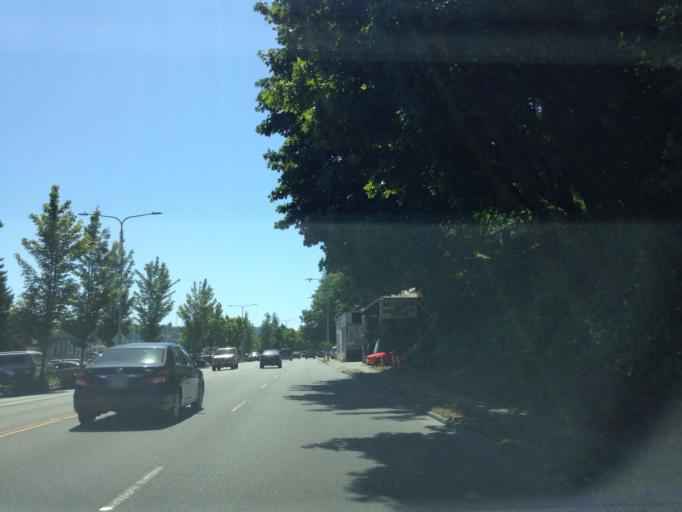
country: US
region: Washington
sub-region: King County
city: Seattle
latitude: 47.6434
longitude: -122.3445
